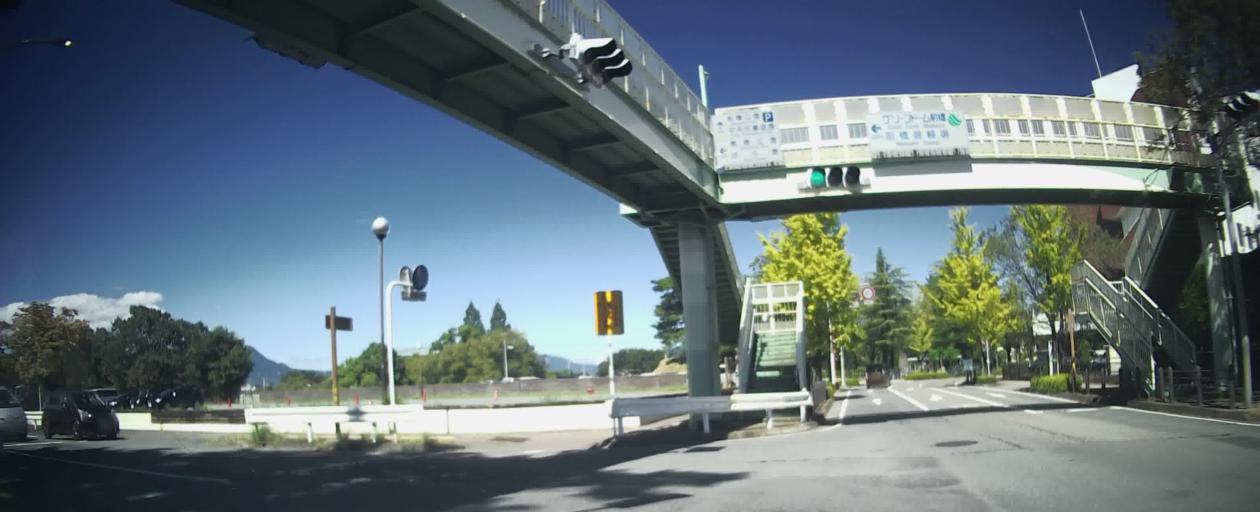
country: JP
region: Gunma
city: Maebashi-shi
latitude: 36.3925
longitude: 139.0617
